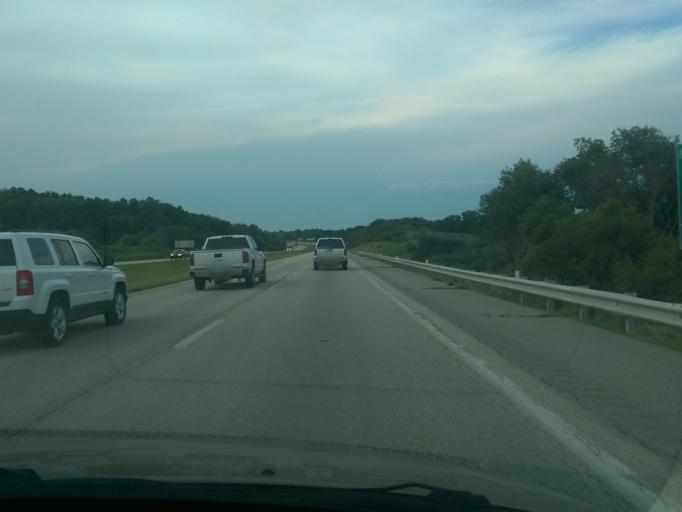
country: US
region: Missouri
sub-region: Andrew County
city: Country Club Village
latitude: 39.8458
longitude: -94.8051
